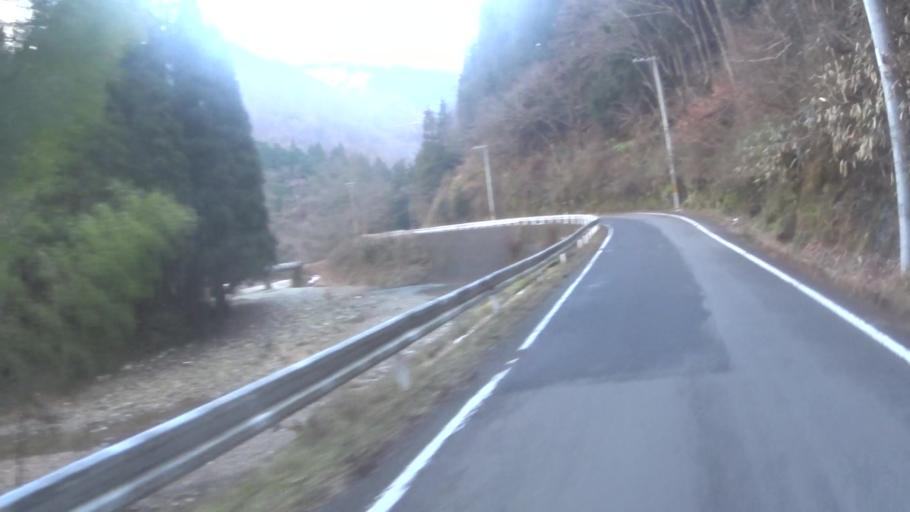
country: JP
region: Kyoto
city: Maizuru
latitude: 35.3874
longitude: 135.4728
